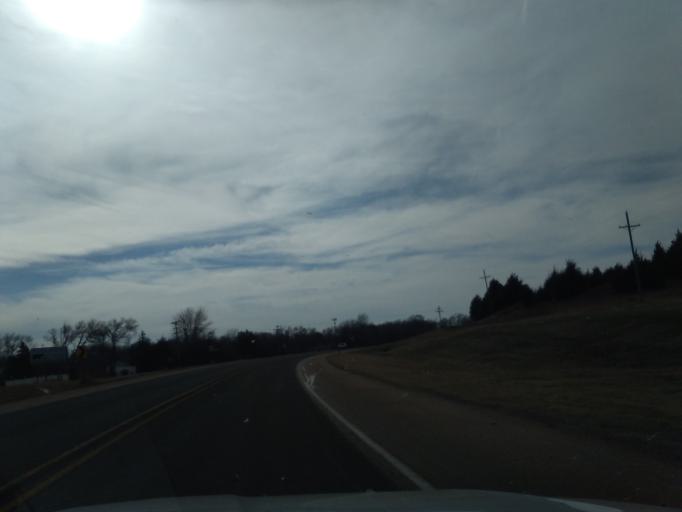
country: US
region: Nebraska
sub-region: Jefferson County
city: Fairbury
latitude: 40.1472
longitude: -97.1631
